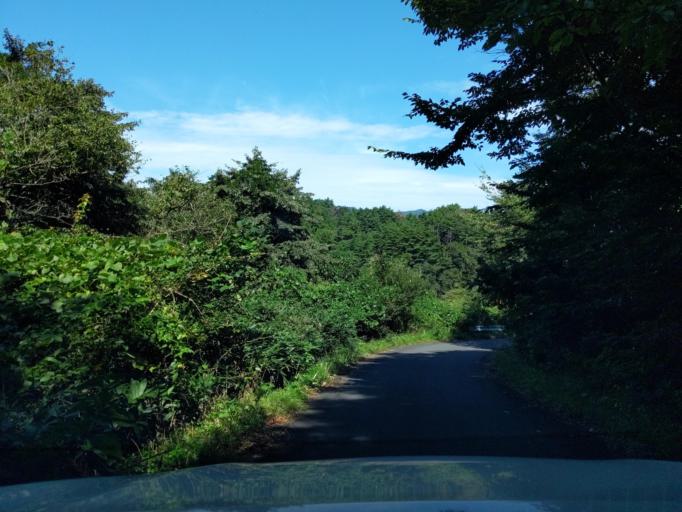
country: JP
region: Fukushima
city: Koriyama
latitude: 37.4017
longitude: 140.2388
